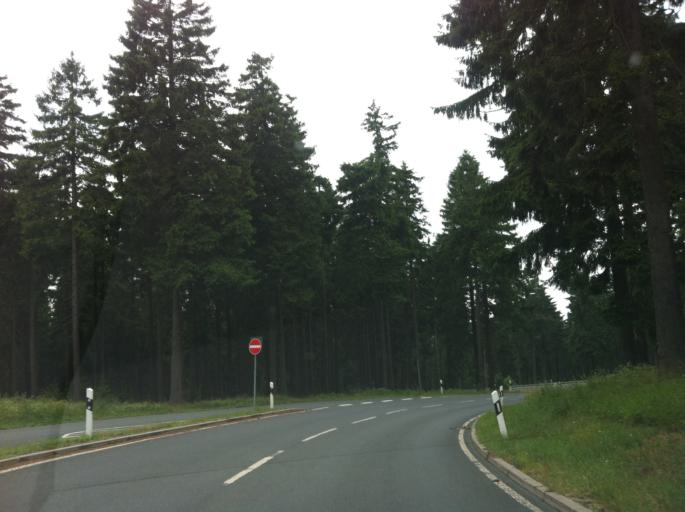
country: DE
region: Hesse
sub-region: Regierungsbezirk Darmstadt
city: Schmitten
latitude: 50.2248
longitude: 8.4511
